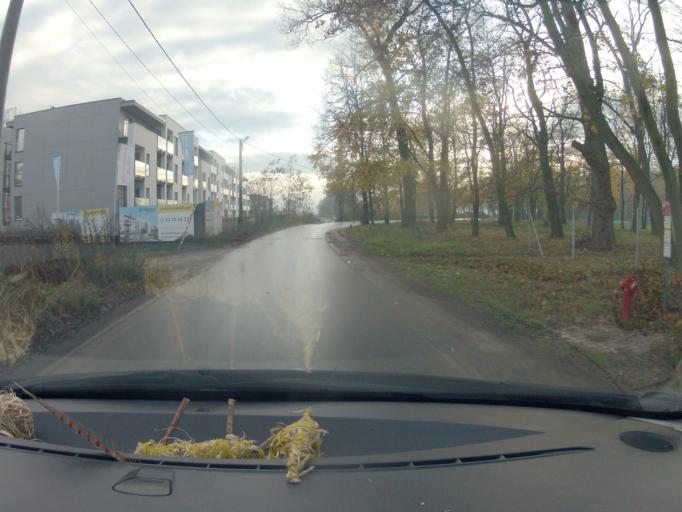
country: PL
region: Lesser Poland Voivodeship
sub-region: Krakow
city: Sidzina
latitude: 50.0029
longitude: 19.8890
